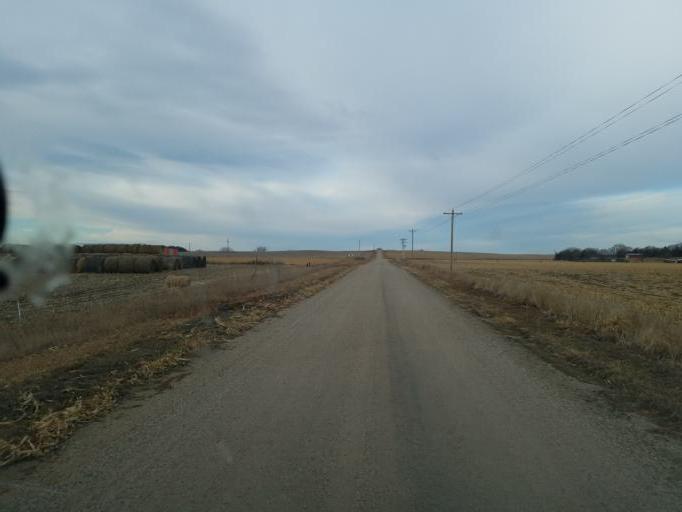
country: US
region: Nebraska
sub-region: Knox County
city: Bloomfield
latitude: 42.5833
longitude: -97.6706
